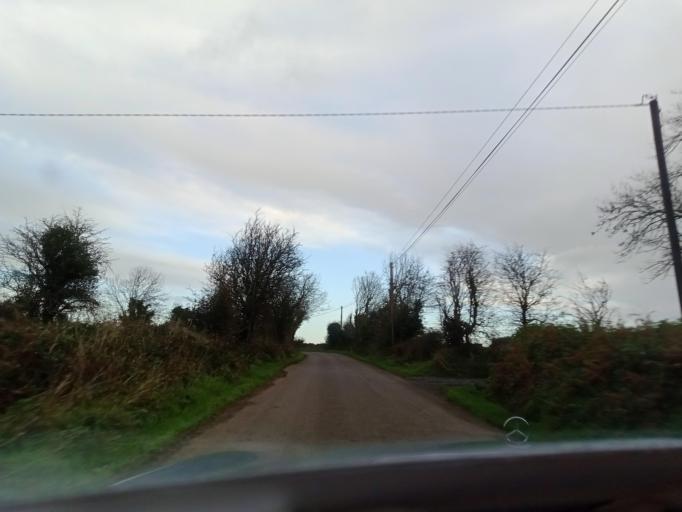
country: IE
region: Munster
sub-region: Waterford
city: Waterford
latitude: 52.3371
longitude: -7.0346
